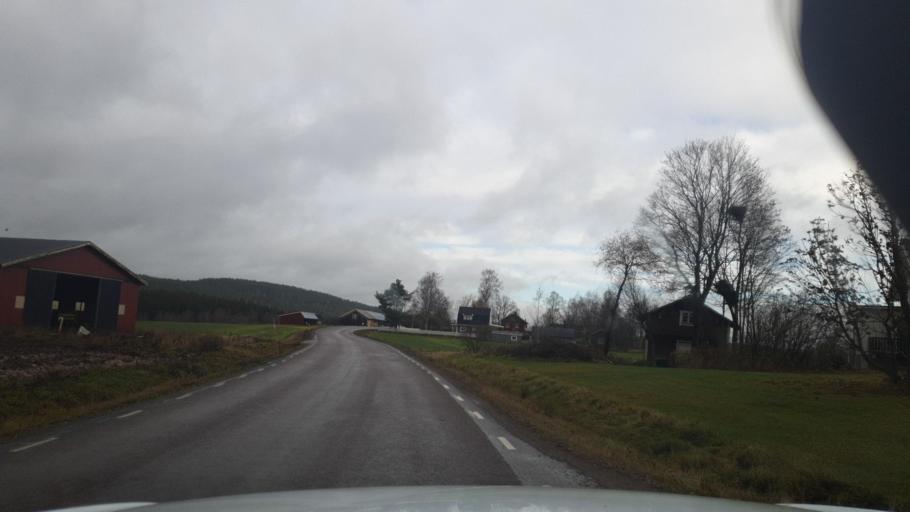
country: SE
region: Vaermland
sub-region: Eda Kommun
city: Charlottenberg
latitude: 59.7670
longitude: 12.1619
